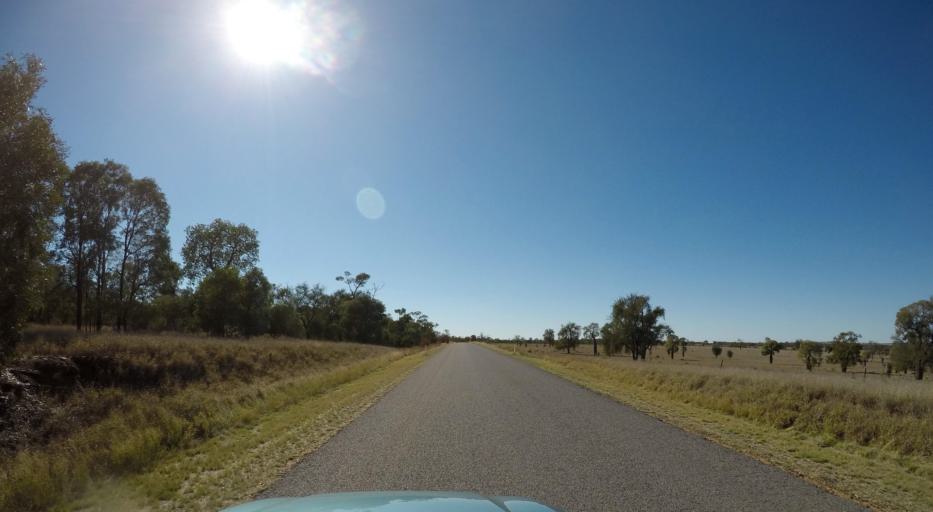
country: AU
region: Queensland
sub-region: Banana
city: Taroom
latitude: -25.7885
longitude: 149.6889
